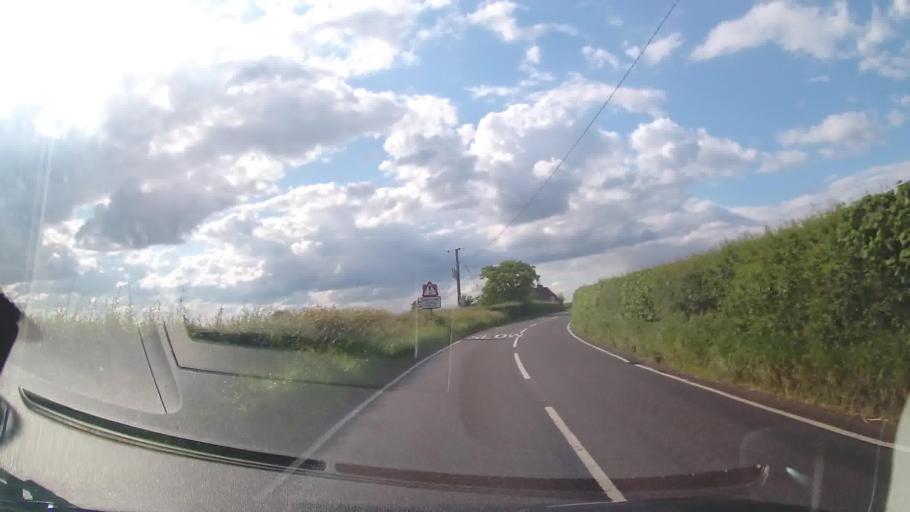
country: GB
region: England
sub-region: Shropshire
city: Harley
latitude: 52.6570
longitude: -2.6156
